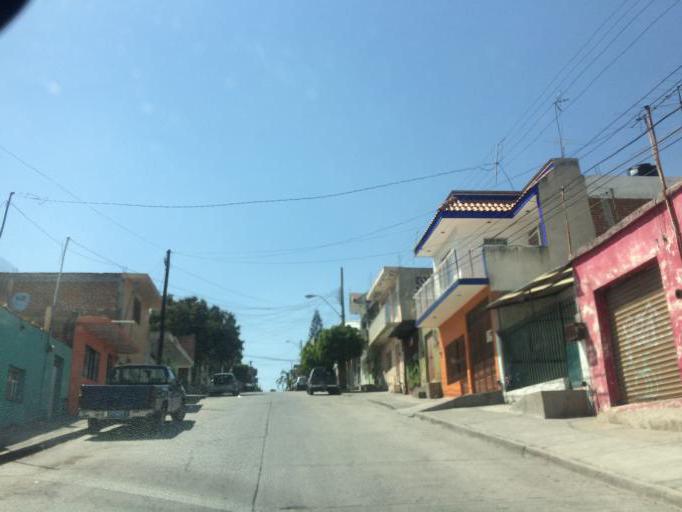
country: MX
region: Guanajuato
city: Leon
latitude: 21.1344
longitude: -101.7008
